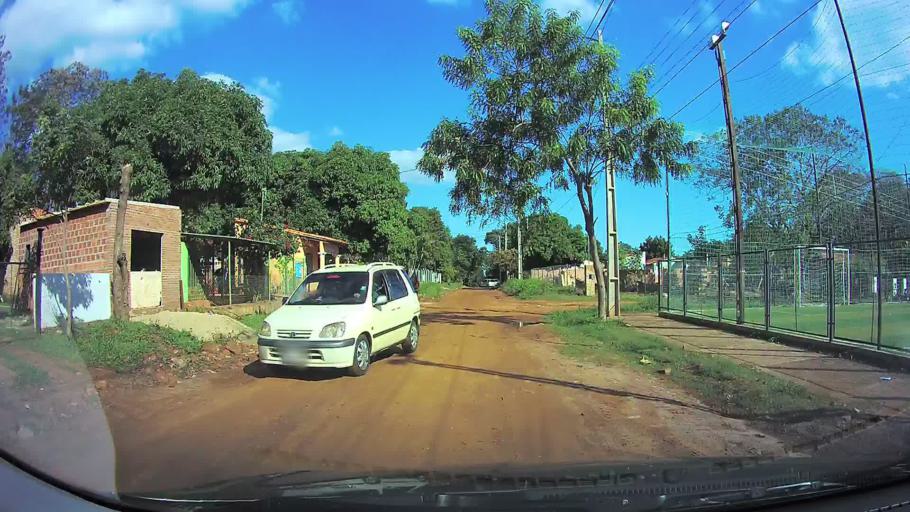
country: PY
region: Central
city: Limpio
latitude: -25.2476
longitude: -57.4746
